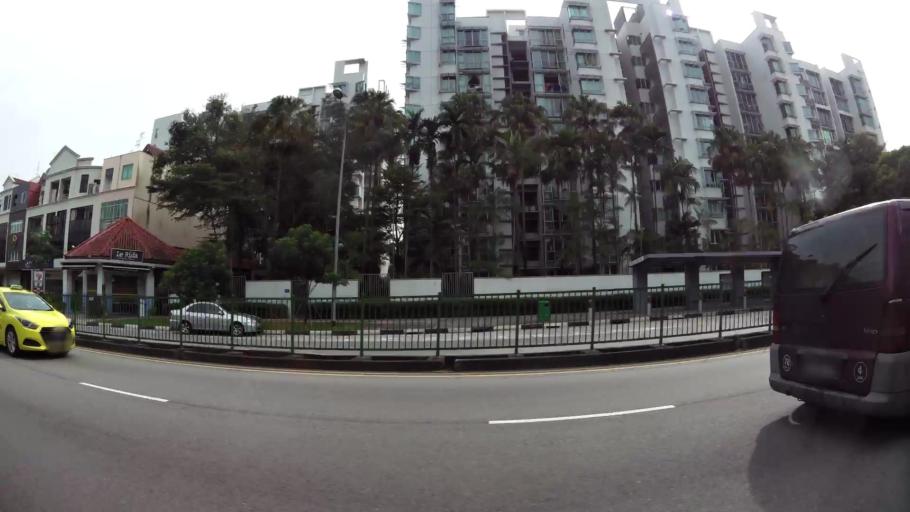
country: SG
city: Singapore
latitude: 1.3335
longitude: 103.7900
